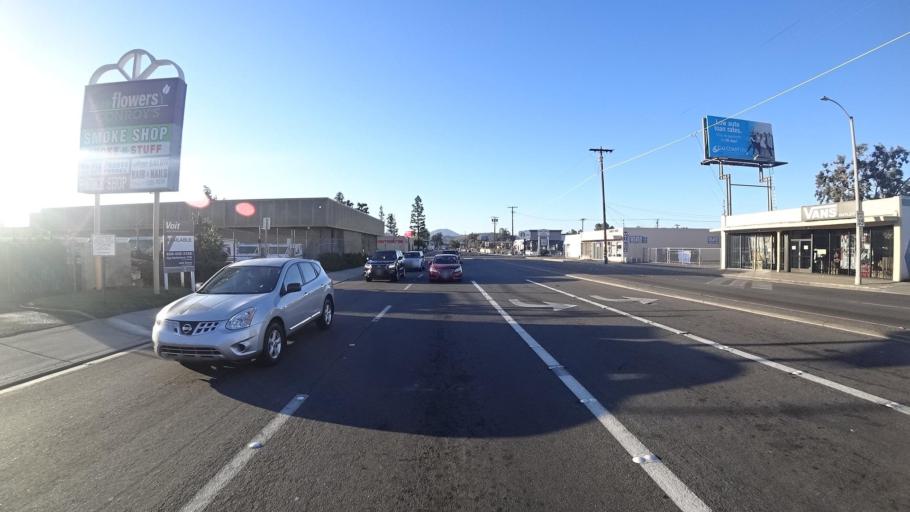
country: US
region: California
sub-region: San Diego County
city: Bostonia
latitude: 32.8072
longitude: -116.9356
